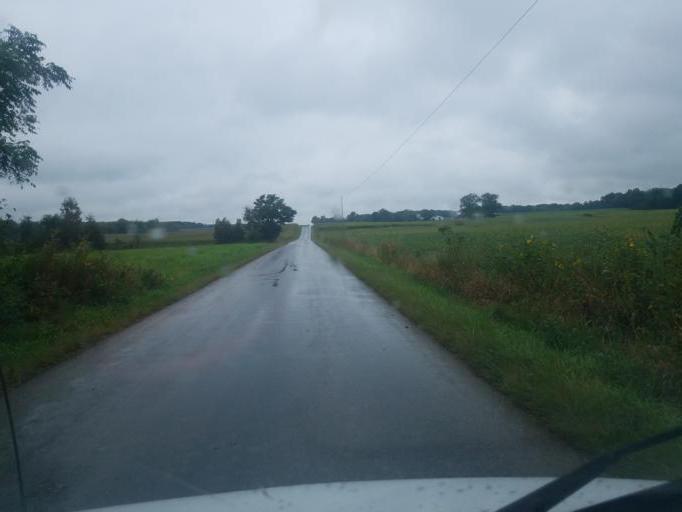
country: US
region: Ohio
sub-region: Wayne County
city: West Salem
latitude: 40.9410
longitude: -82.1150
